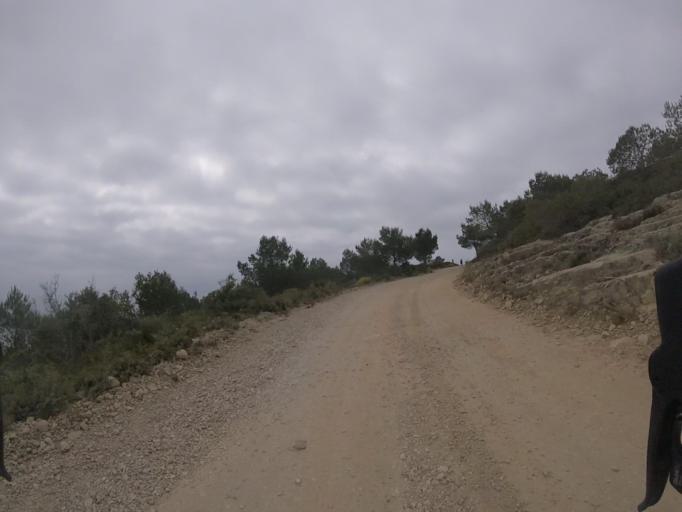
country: ES
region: Valencia
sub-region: Provincia de Castello
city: Peniscola
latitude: 40.3235
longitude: 0.3633
